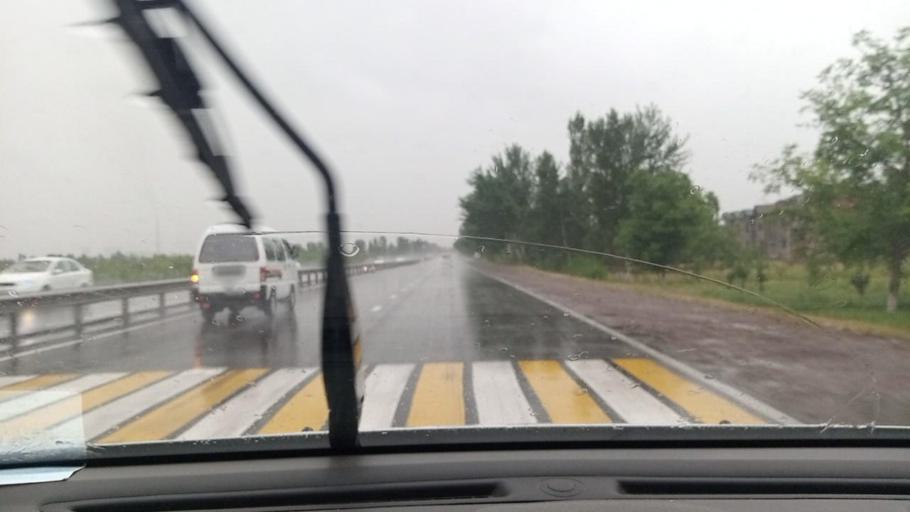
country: UZ
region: Toshkent
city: Ohangaron
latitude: 40.9098
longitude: 69.7520
